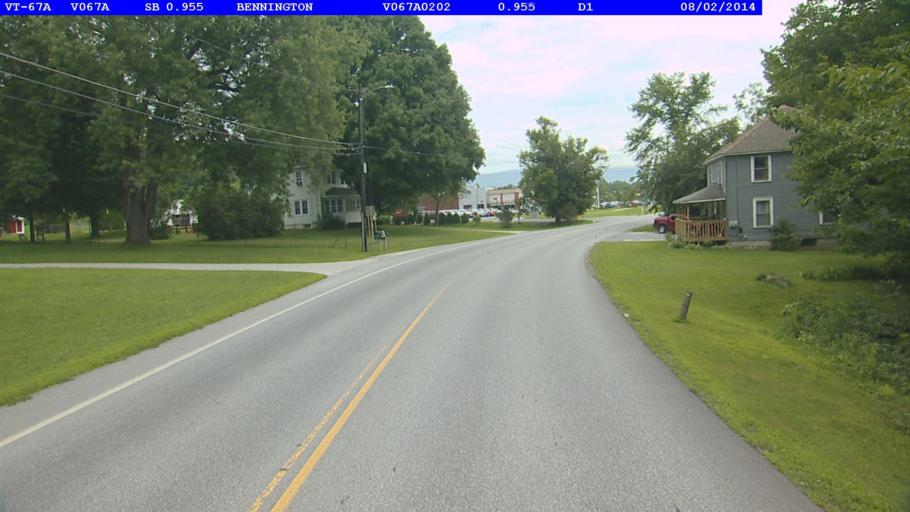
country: US
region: Vermont
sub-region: Bennington County
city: North Bennington
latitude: 42.9117
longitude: -73.2233
